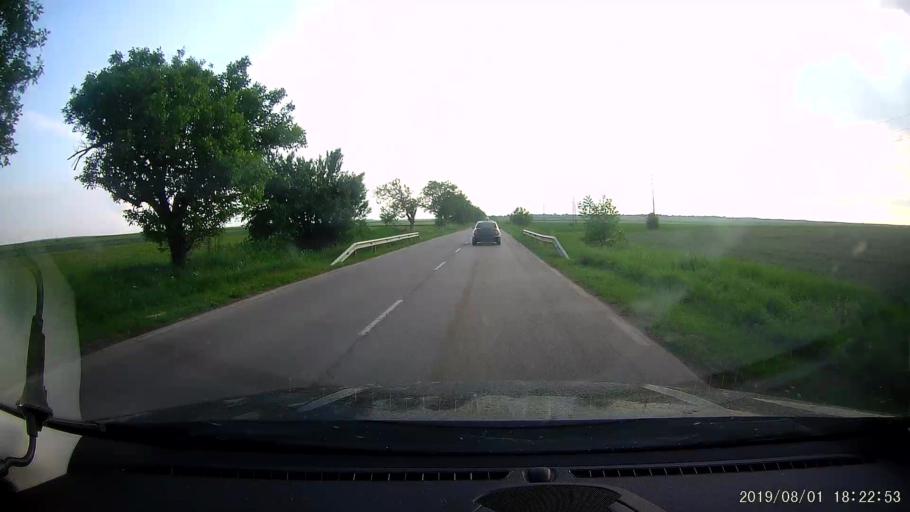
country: BG
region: Shumen
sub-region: Obshtina Kaolinovo
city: Kaolinovo
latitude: 43.6367
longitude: 27.0396
